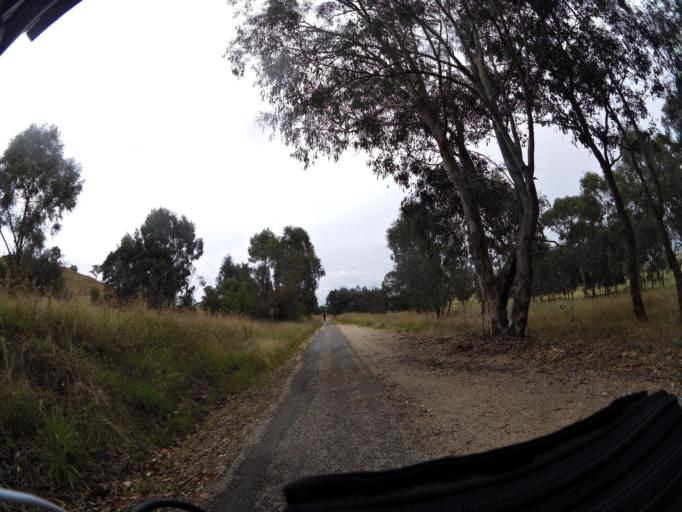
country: AU
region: New South Wales
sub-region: Albury Municipality
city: East Albury
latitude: -36.2240
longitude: 147.1080
